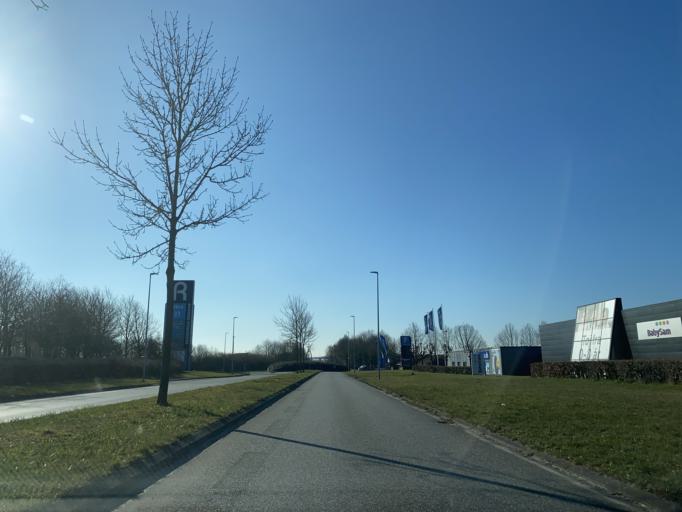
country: DK
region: Central Jutland
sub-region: Randers Kommune
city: Randers
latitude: 56.4293
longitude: 10.0614
